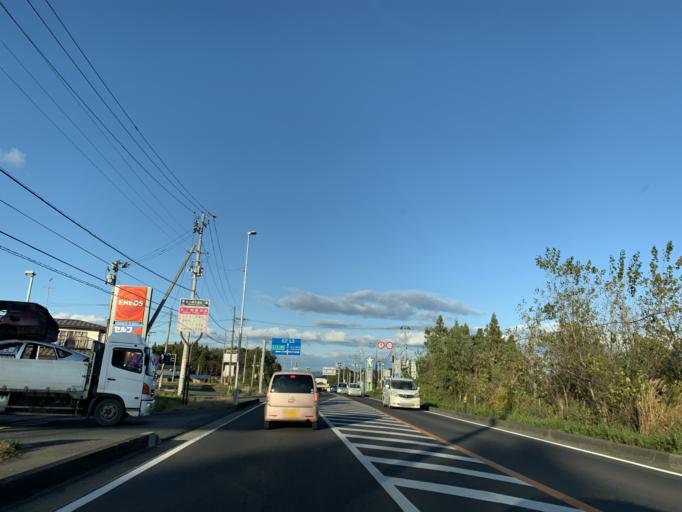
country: JP
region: Iwate
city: Kitakami
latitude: 39.2352
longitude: 141.0939
